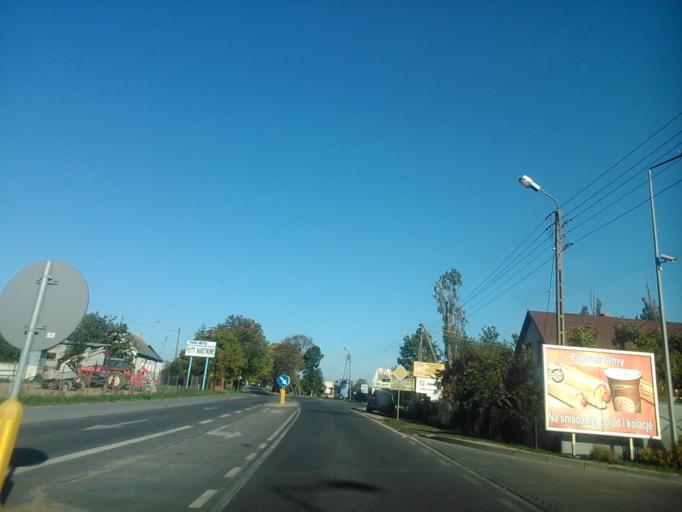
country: PL
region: Kujawsko-Pomorskie
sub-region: Powiat golubsko-dobrzynski
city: Golub-Dobrzyn
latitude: 53.1223
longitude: 19.0441
